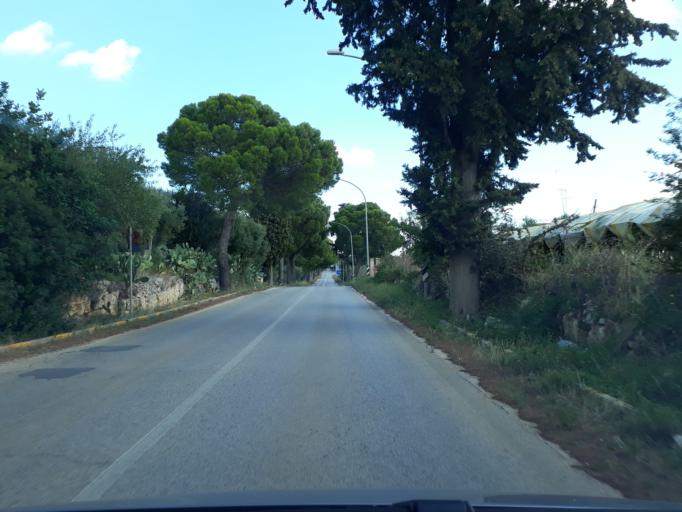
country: IT
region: Apulia
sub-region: Provincia di Bari
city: Rutigliano
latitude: 41.0256
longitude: 17.0332
